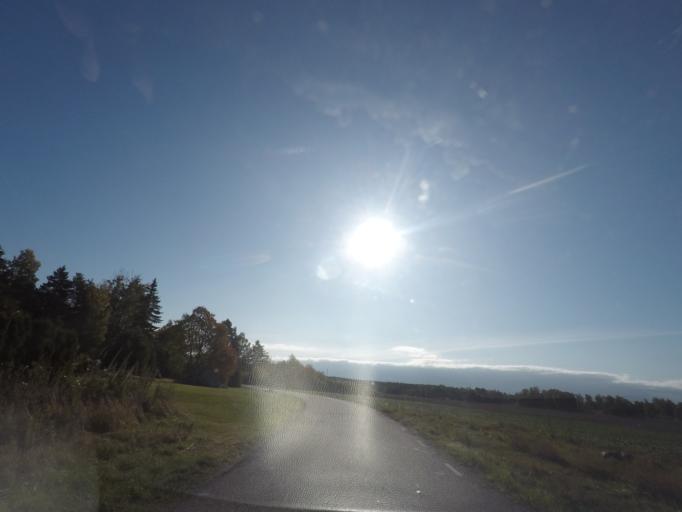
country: SE
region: Vaestmanland
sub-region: Hallstahammars Kommun
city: Kolback
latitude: 59.5496
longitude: 16.3433
